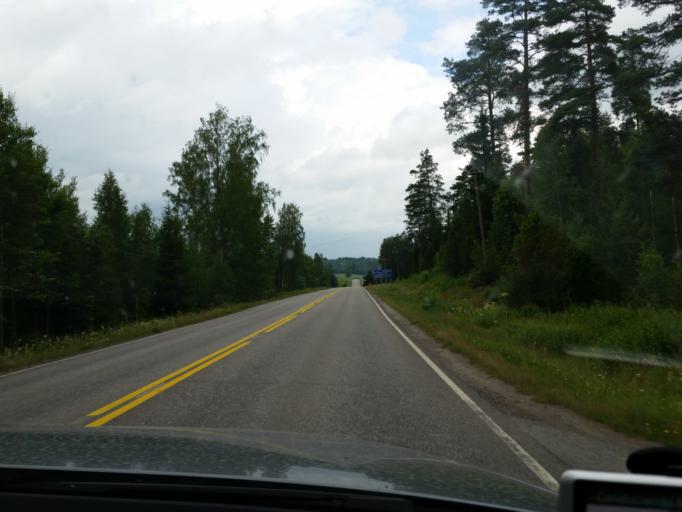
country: FI
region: Uusimaa
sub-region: Helsinki
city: Saukkola
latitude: 60.3973
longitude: 24.0702
